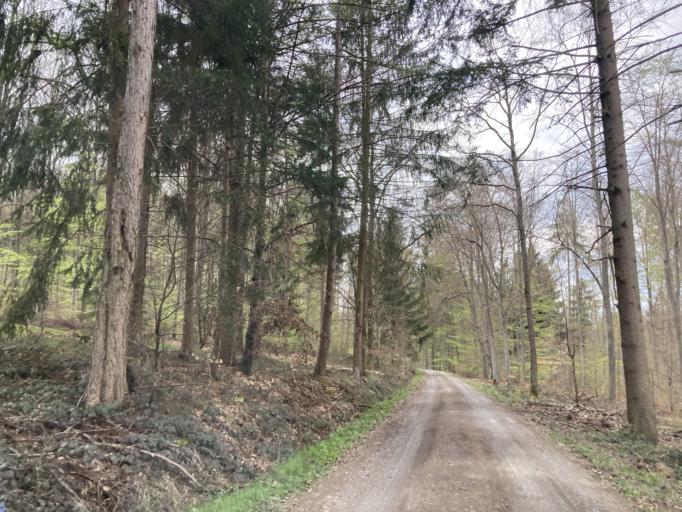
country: DE
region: Baden-Wuerttemberg
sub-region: Tuebingen Region
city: Dettenhausen
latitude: 48.5943
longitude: 9.1289
